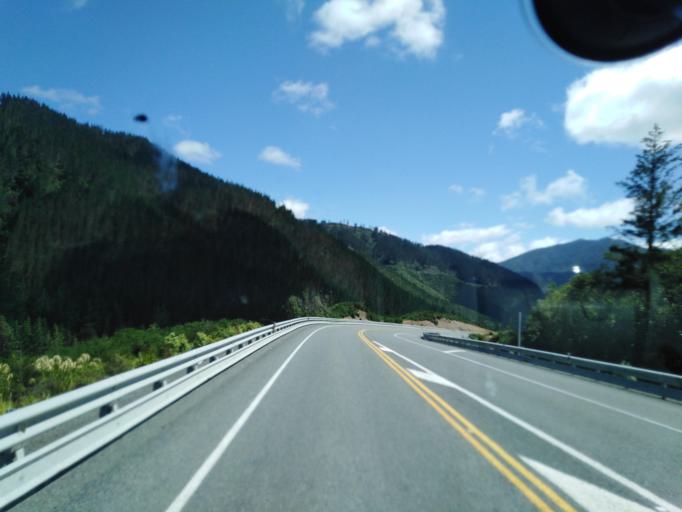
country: NZ
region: Nelson
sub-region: Nelson City
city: Nelson
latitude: -41.1895
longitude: 173.5539
